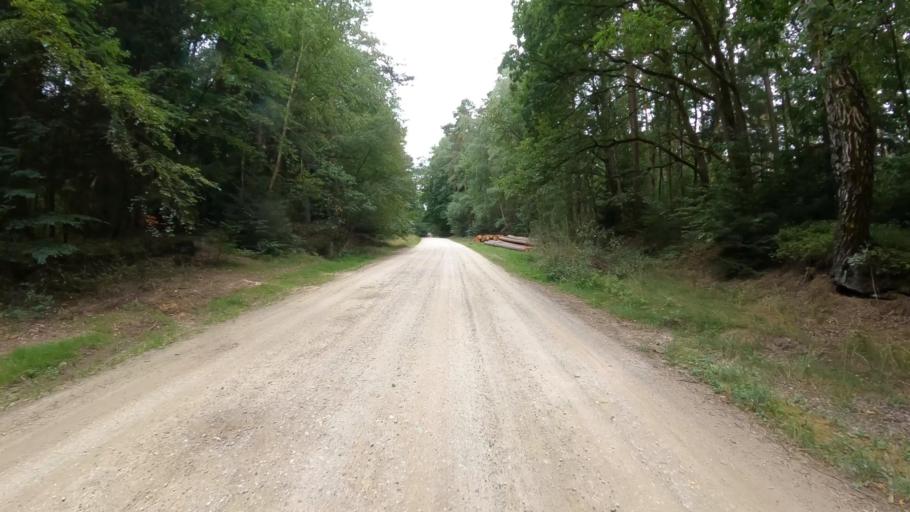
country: DE
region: Lower Saxony
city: Kakenstorf
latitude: 53.3167
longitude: 9.7402
